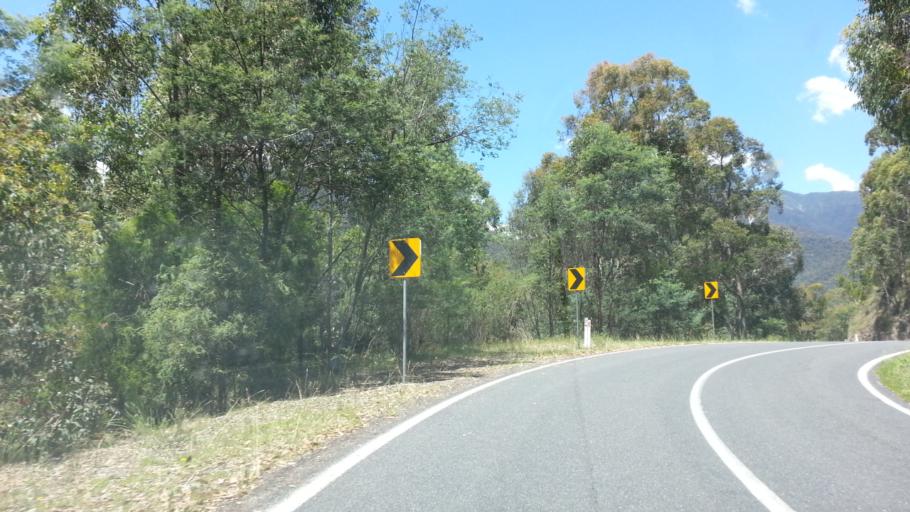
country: AU
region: Victoria
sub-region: Alpine
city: Mount Beauty
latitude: -36.7576
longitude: 147.2049
